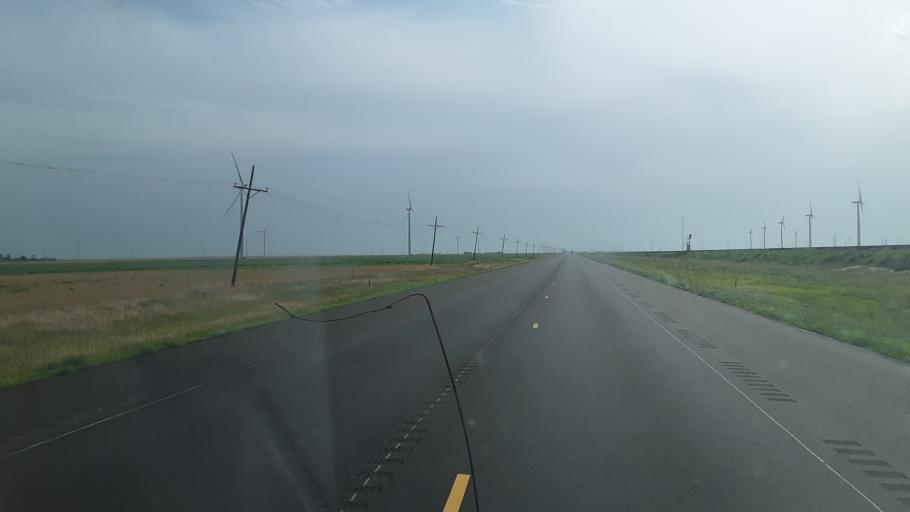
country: US
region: Kansas
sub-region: Ford County
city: Dodge City
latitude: 37.8062
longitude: -99.8461
